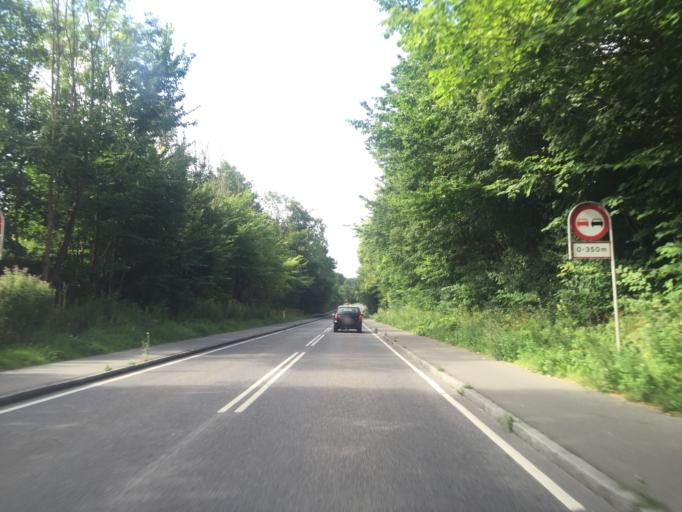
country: DK
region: South Denmark
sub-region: Svendborg Kommune
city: Thuro By
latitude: 55.1019
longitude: 10.7089
